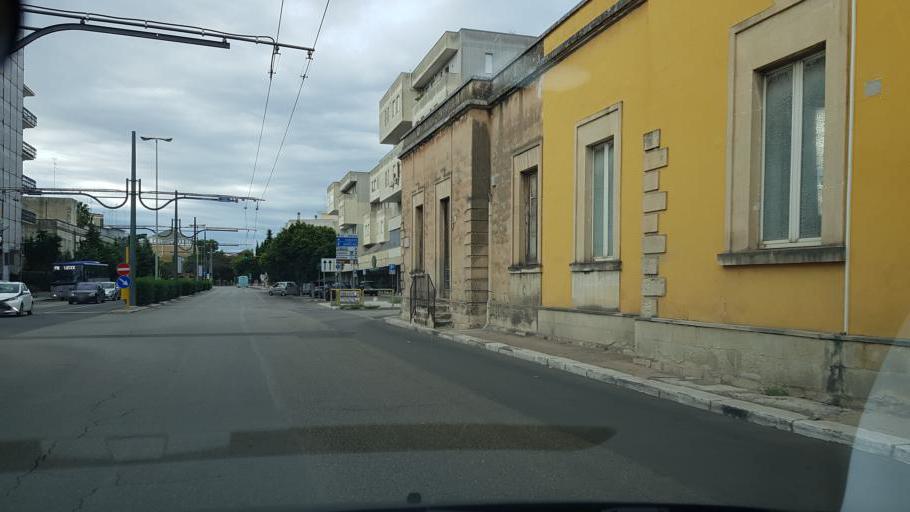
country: IT
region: Apulia
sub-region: Provincia di Lecce
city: Lecce
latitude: 40.3623
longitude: 18.1770
